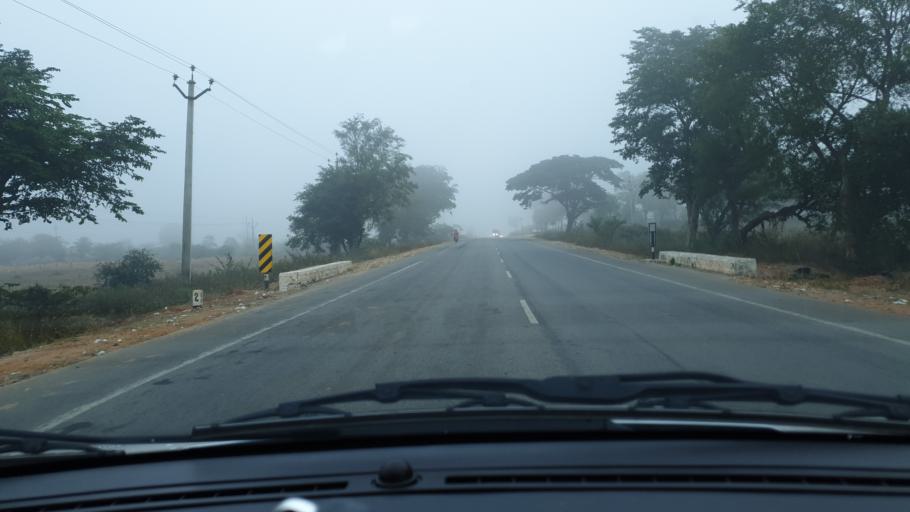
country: IN
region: Telangana
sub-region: Mahbubnagar
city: Nagar Karnul
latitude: 16.6632
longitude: 78.5686
